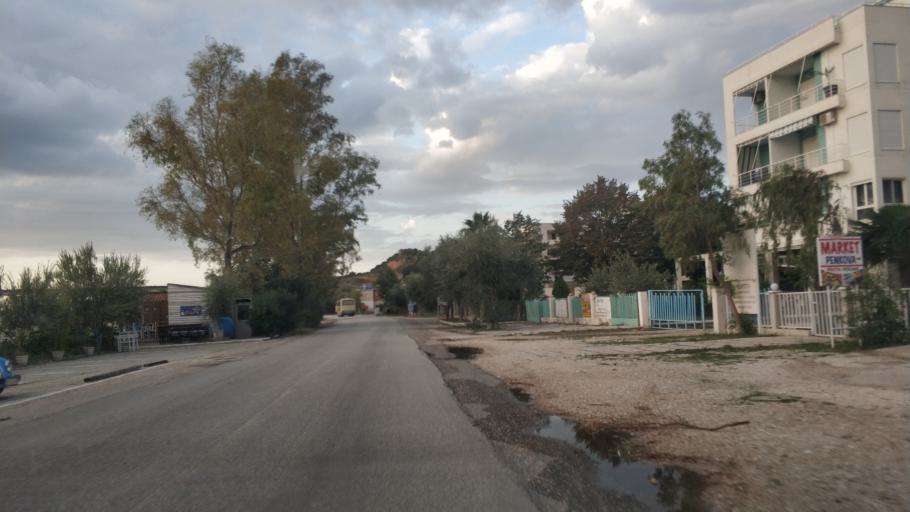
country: AL
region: Vlore
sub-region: Rrethi i Vlores
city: Orikum
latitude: 40.3570
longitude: 19.4830
